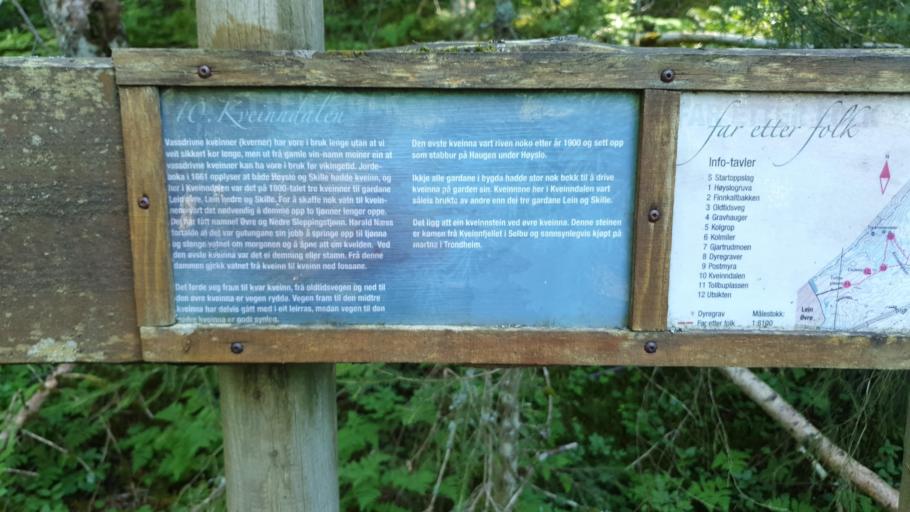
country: NO
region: Nord-Trondelag
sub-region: Levanger
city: Levanger
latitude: 63.6909
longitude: 11.2644
